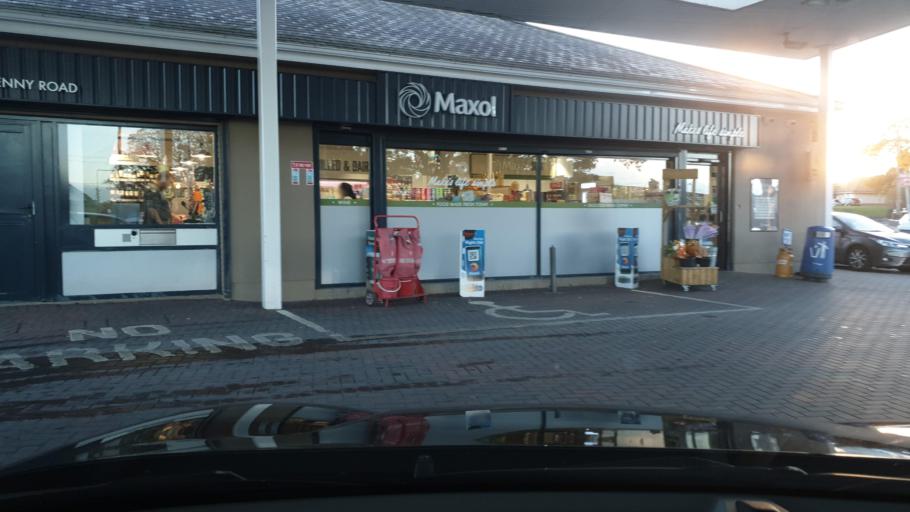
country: IE
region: Leinster
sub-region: Lu
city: Drogheda
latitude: 53.7228
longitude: -6.3480
